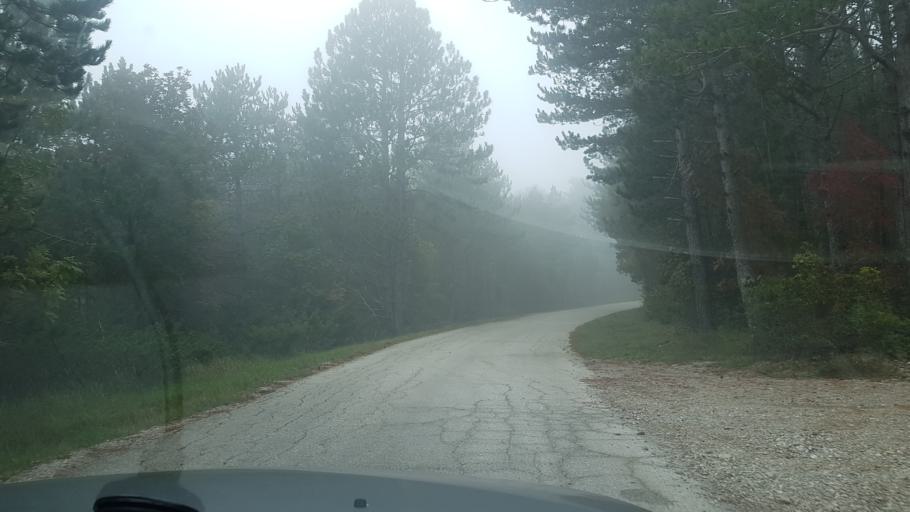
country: HR
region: Istarska
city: Buzet
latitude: 45.4513
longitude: 14.0287
